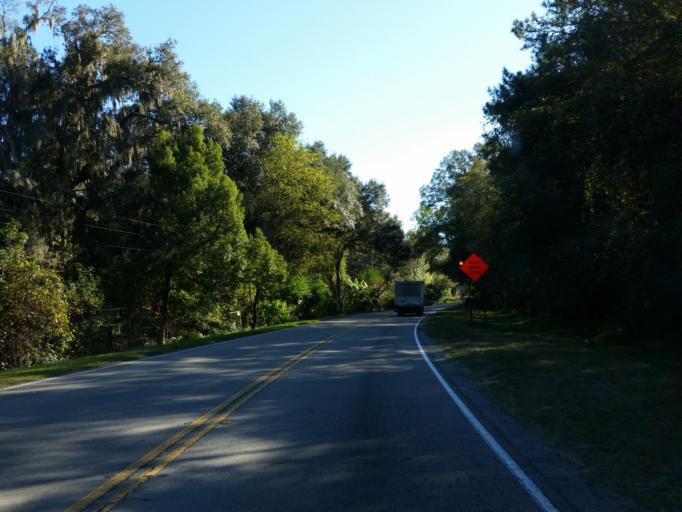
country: US
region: Florida
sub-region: Alachua County
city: Gainesville
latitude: 29.5036
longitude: -82.2905
